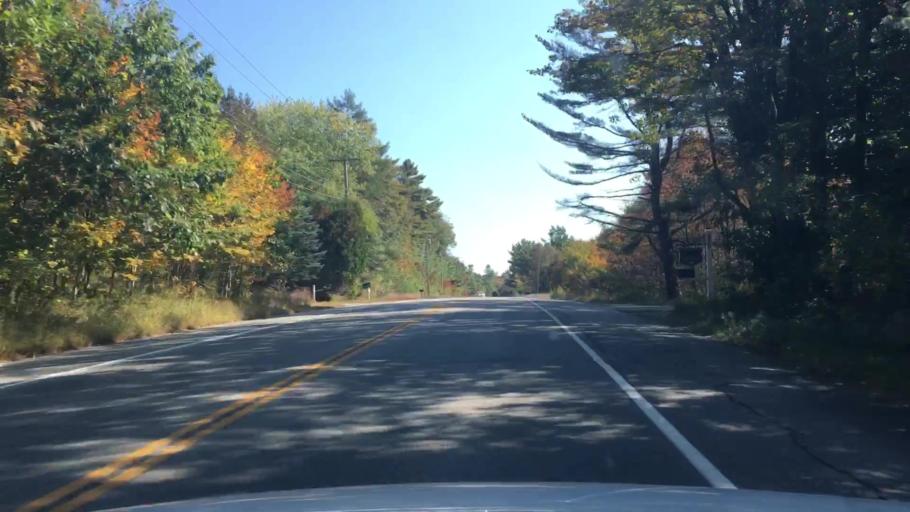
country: US
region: Maine
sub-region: Androscoggin County
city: Lisbon Falls
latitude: 43.9802
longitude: -70.0308
